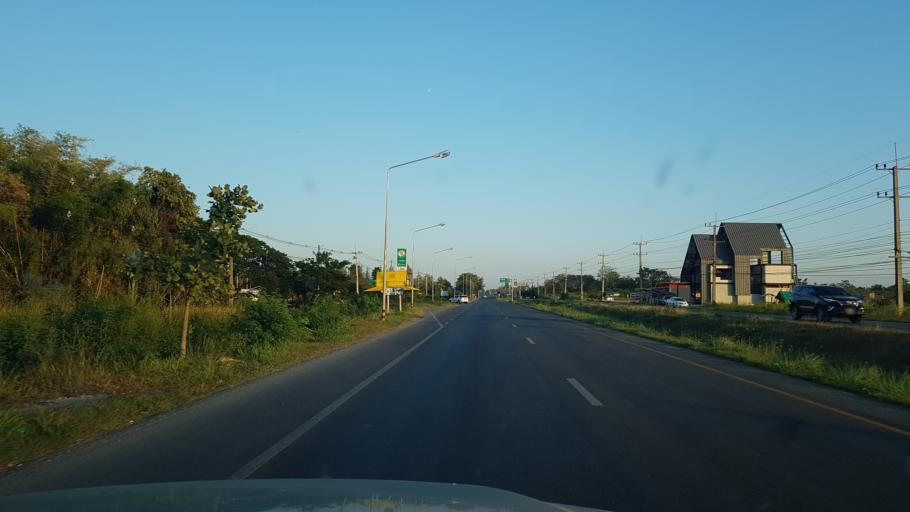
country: TH
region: Khon Kaen
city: Chum Phae
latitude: 16.5815
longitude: 102.0169
